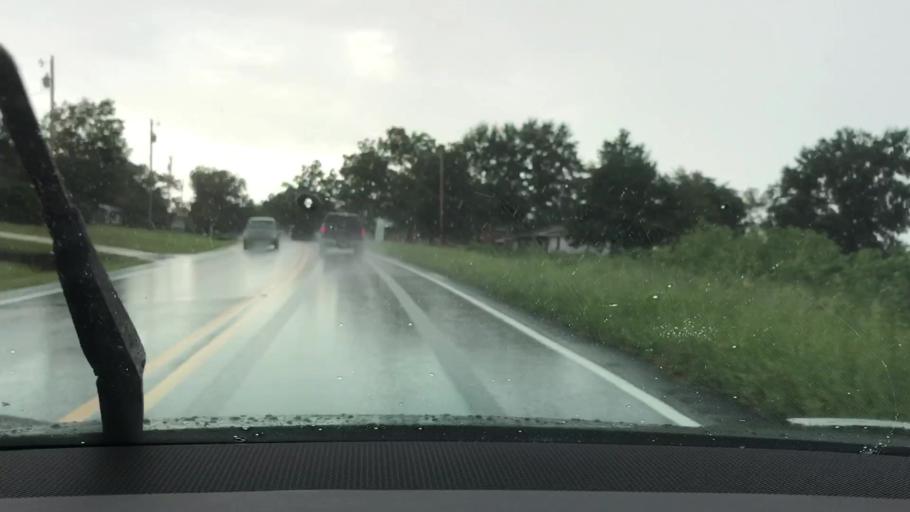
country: US
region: Alabama
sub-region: Covington County
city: Opp
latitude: 31.2175
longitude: -86.1656
